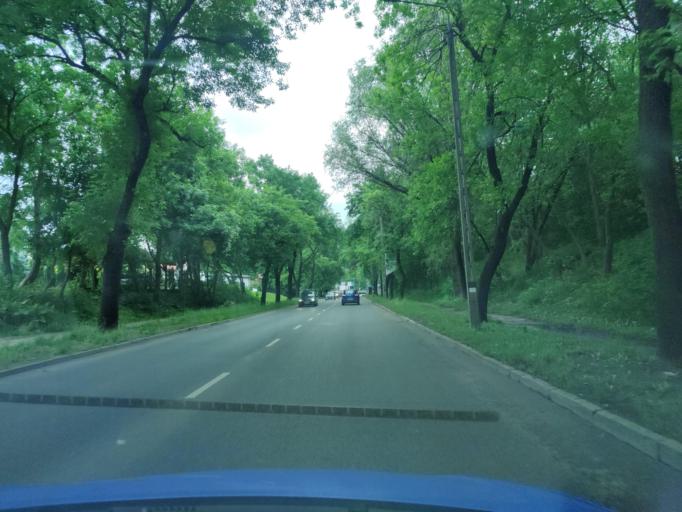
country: PL
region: Silesian Voivodeship
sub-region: Sosnowiec
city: Sosnowiec
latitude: 50.2710
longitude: 19.1469
